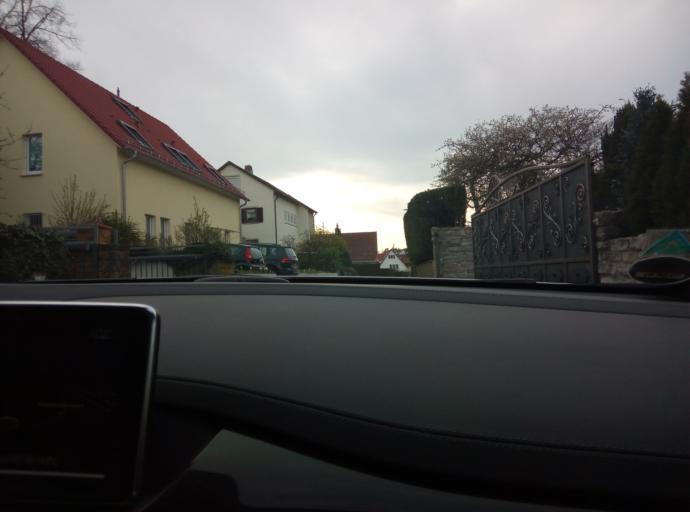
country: DE
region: Baden-Wuerttemberg
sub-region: Tuebingen Region
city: Rottenburg
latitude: 48.4708
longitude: 8.9351
